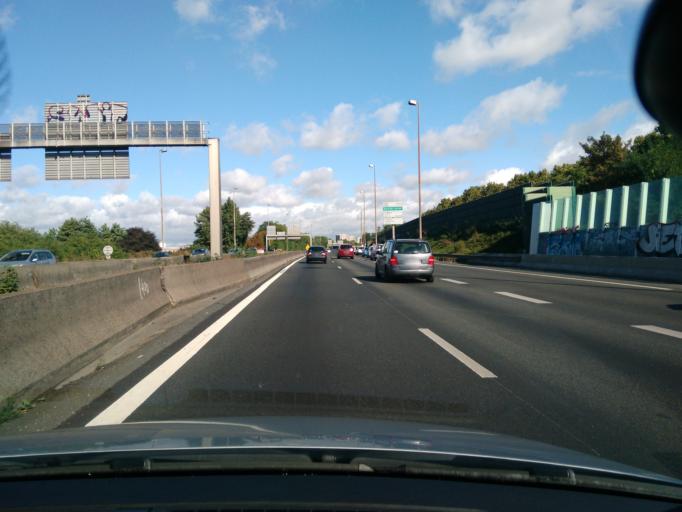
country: FR
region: Ile-de-France
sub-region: Departement du Val-de-Marne
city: Maisons-Alfort
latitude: 48.7854
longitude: 2.4403
